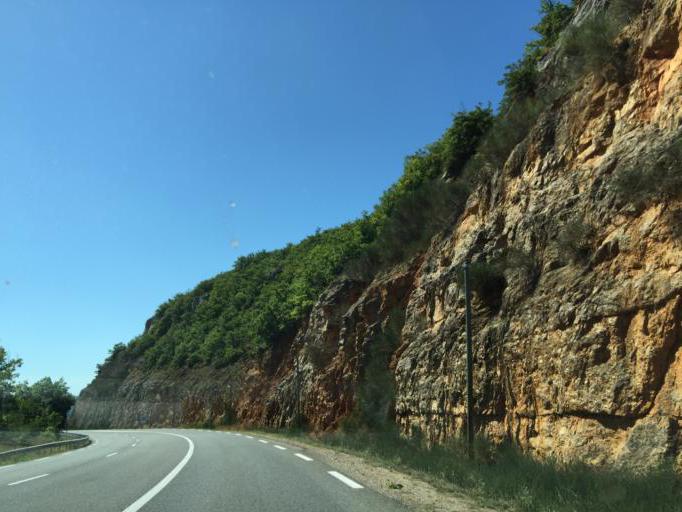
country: FR
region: Midi-Pyrenees
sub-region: Departement de l'Aveyron
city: Creissels
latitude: 44.0158
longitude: 3.0460
